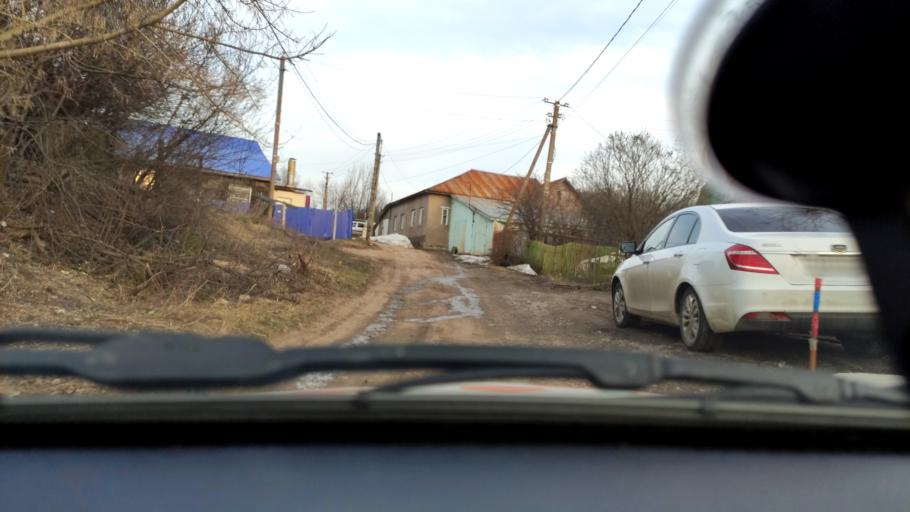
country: RU
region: Bashkortostan
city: Ufa
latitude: 54.8306
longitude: 56.1459
